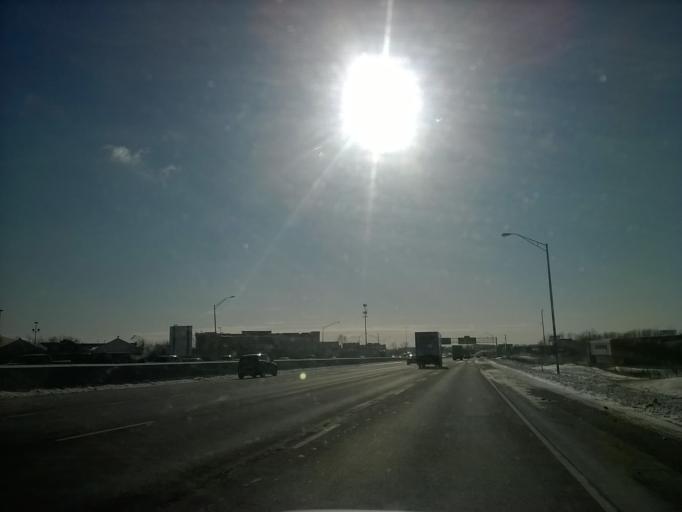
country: US
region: Indiana
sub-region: Hamilton County
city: Fishers
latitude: 39.9020
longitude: -86.0485
